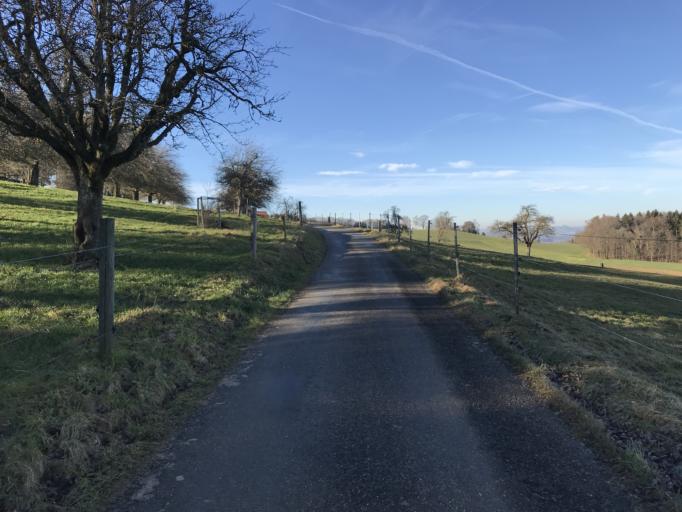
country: CH
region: Thurgau
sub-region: Frauenfeld District
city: Eschenz
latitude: 47.6310
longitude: 8.8599
